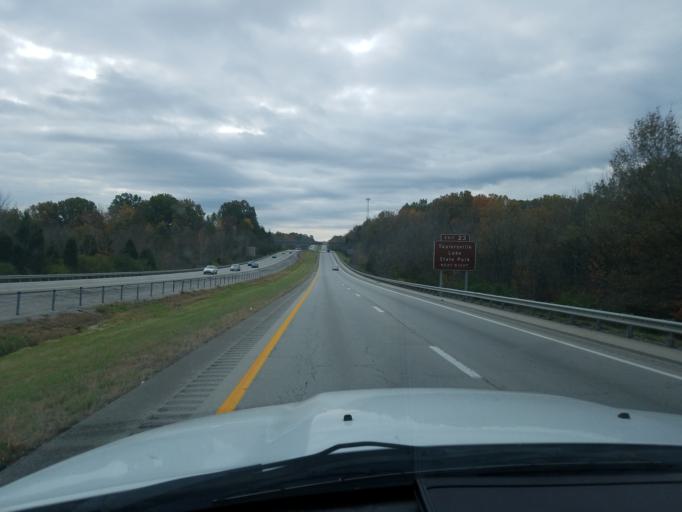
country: US
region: Kentucky
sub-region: Jefferson County
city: Middletown
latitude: 38.2093
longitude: -85.5071
